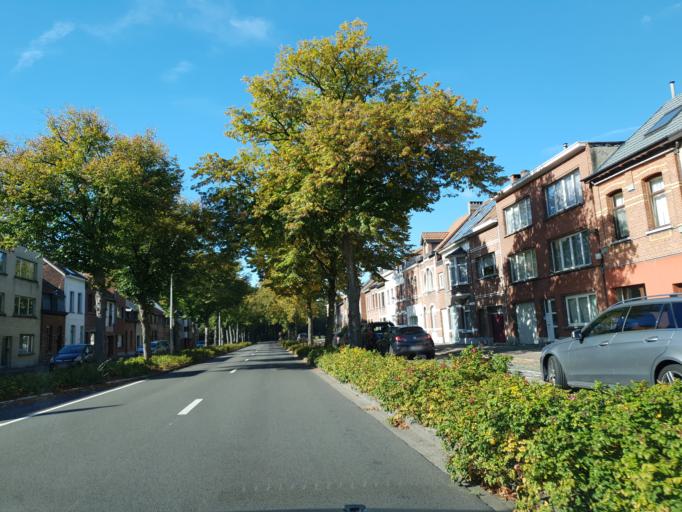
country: BE
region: Flanders
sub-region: Provincie Antwerpen
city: Schoten
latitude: 51.2494
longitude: 4.4825
